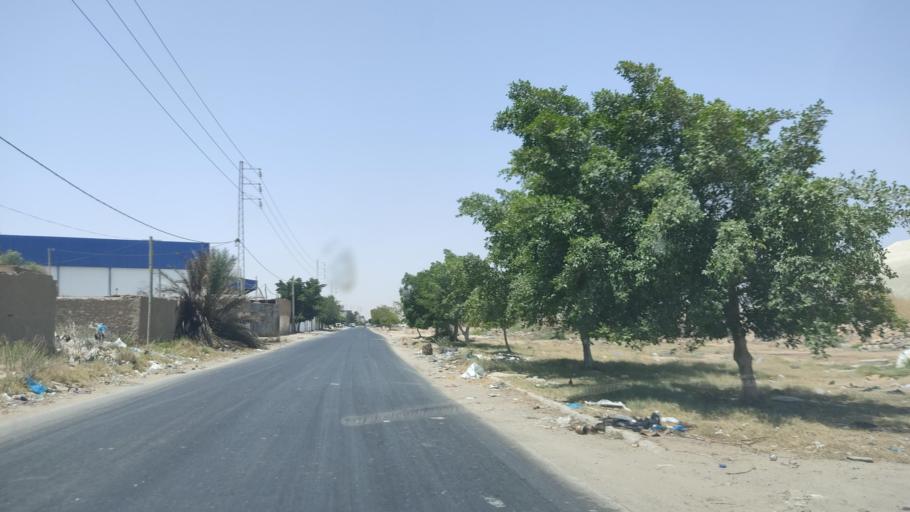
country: TN
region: Safaqis
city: Sfax
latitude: 34.6930
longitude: 10.7266
